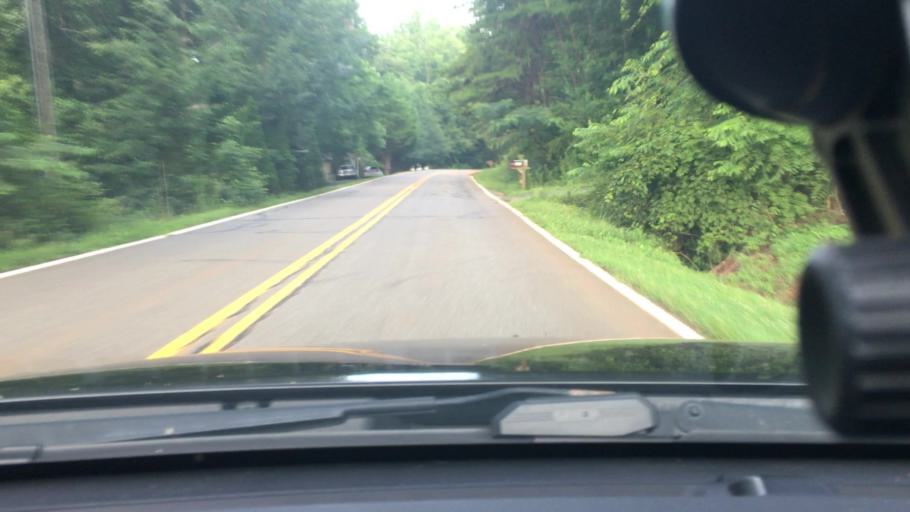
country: US
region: North Carolina
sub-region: Rutherford County
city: Rutherfordton
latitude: 35.3765
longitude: -81.9858
